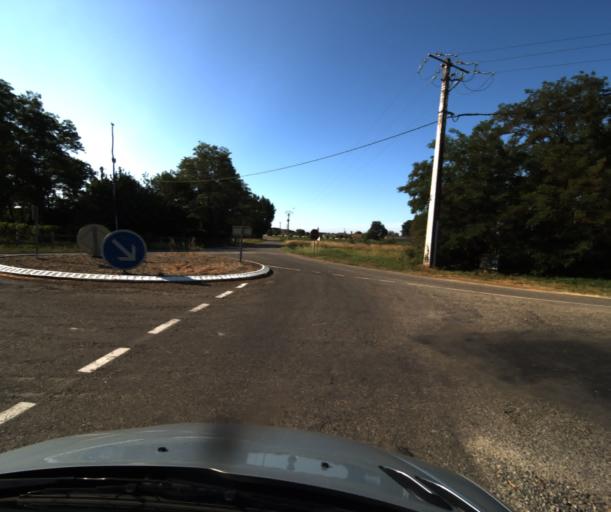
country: FR
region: Midi-Pyrenees
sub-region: Departement du Tarn-et-Garonne
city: Saint-Porquier
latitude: 44.0444
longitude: 1.2150
